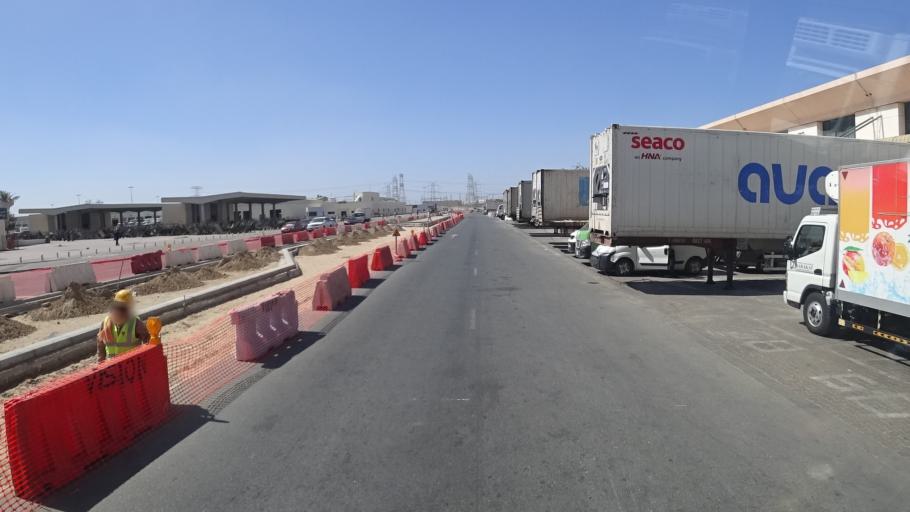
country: AE
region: Ash Shariqah
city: Sharjah
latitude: 25.1726
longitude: 55.3910
